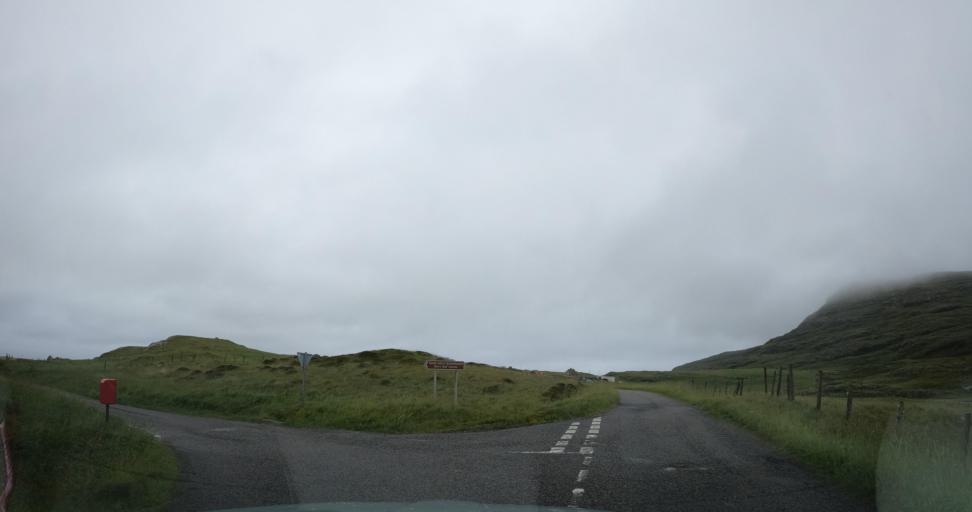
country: GB
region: Scotland
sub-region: Eilean Siar
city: Barra
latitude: 57.0029
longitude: -7.4796
